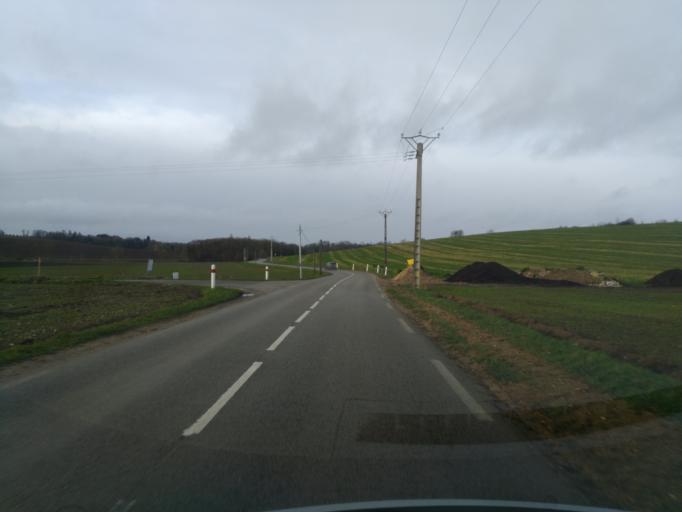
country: FR
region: Ile-de-France
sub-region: Departement des Yvelines
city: Saint-Nom-la-Breteche
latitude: 48.8368
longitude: 2.0323
